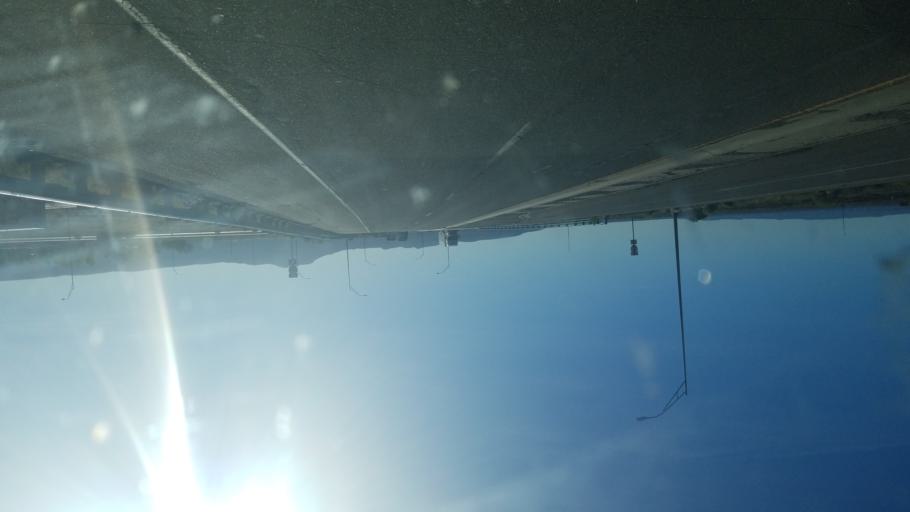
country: US
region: New Mexico
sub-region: Cibola County
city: Grants
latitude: 35.1248
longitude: -107.8290
